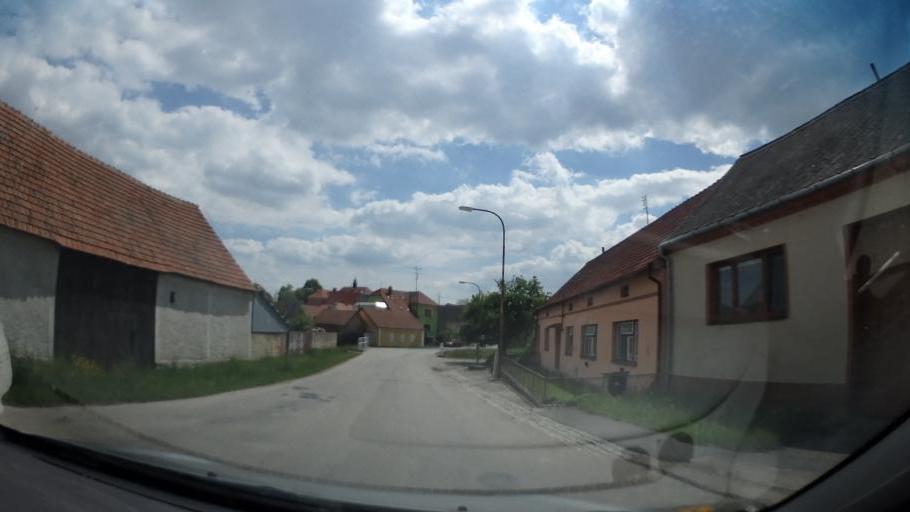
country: CZ
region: Vysocina
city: Mohelno
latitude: 49.1155
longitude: 16.1886
